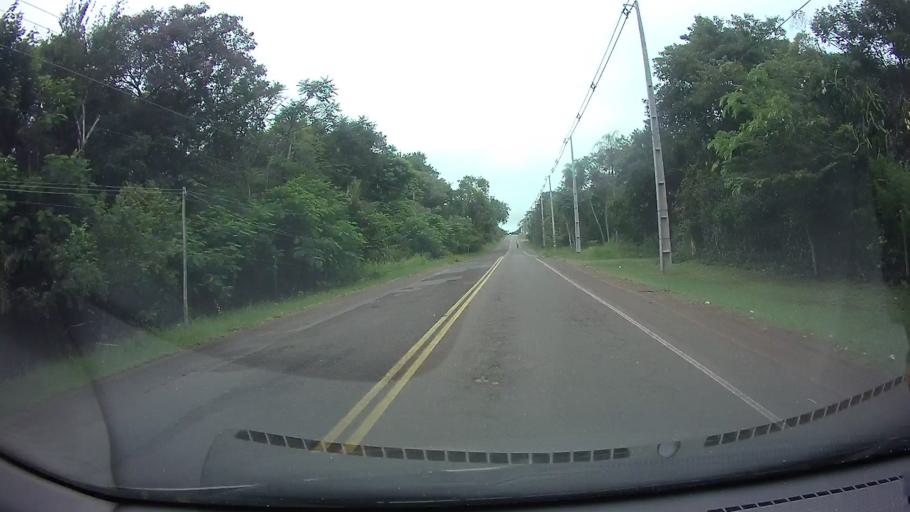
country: PY
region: Cordillera
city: Altos
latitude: -25.2757
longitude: -57.2607
